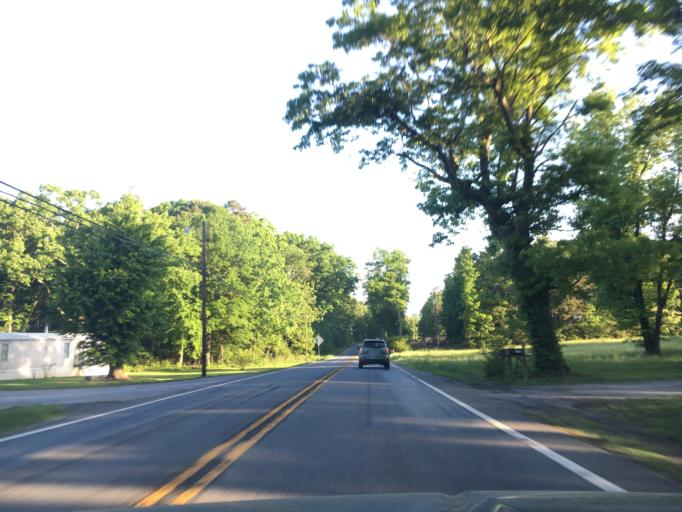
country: US
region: Virginia
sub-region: Campbell County
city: Rustburg
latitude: 37.2555
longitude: -79.1210
